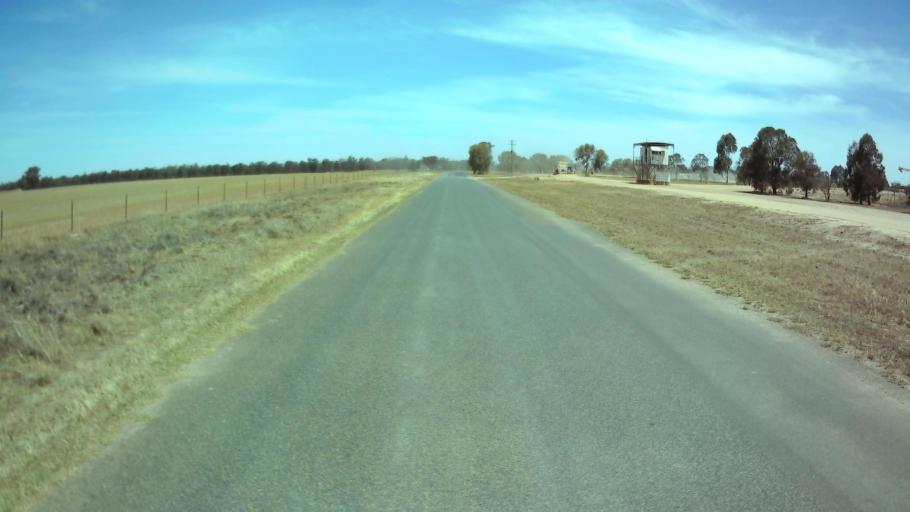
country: AU
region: New South Wales
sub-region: Weddin
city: Grenfell
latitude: -33.8333
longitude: 147.7459
